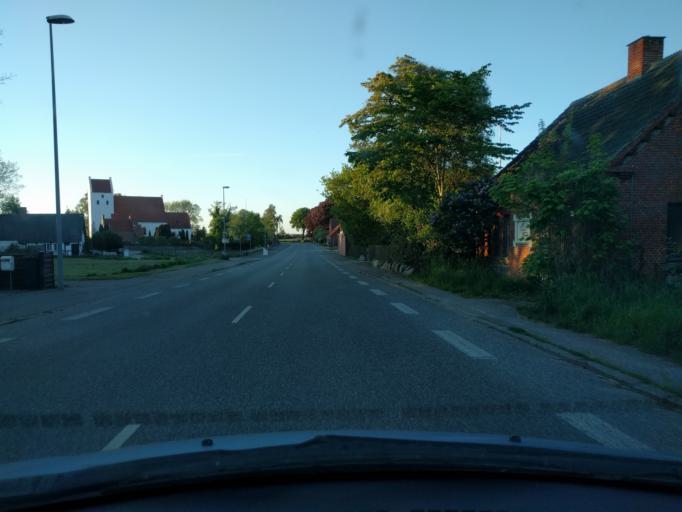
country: DK
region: Zealand
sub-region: Guldborgsund Kommune
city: Stubbekobing
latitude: 54.8037
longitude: 11.9937
